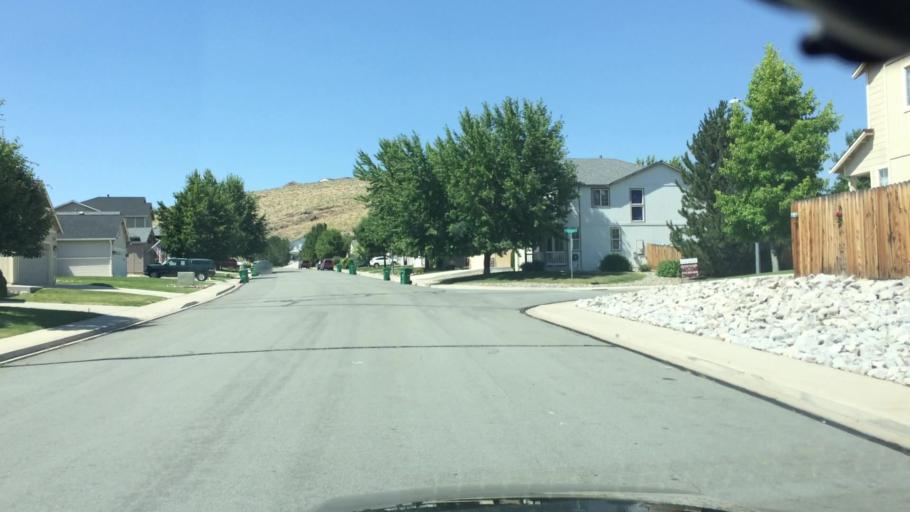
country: US
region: Nevada
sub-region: Washoe County
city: Sparks
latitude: 39.5701
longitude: -119.6929
